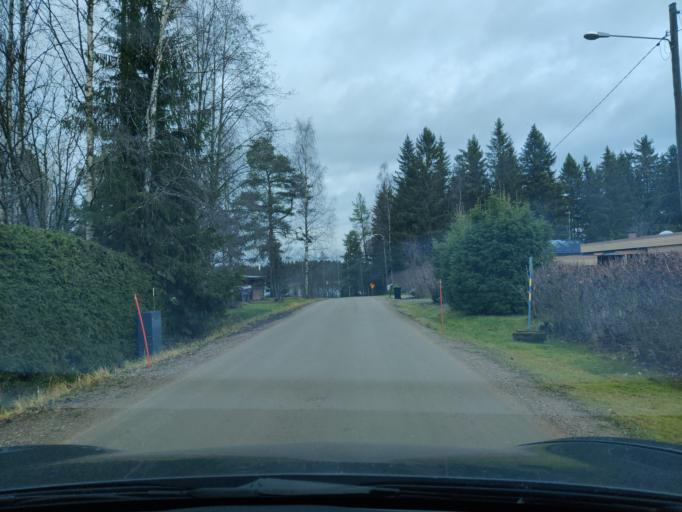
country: FI
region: Northern Savo
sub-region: Ylae-Savo
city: Kiuruvesi
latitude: 63.6458
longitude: 26.6400
